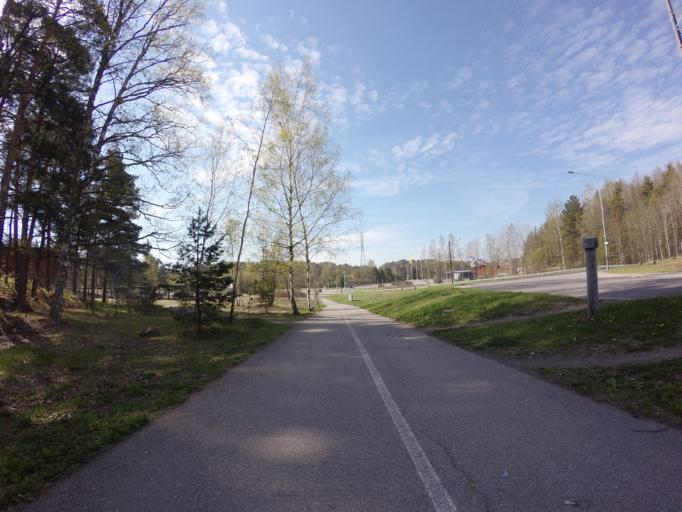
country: FI
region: Varsinais-Suomi
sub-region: Turku
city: Raisio
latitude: 60.4542
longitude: 22.1571
